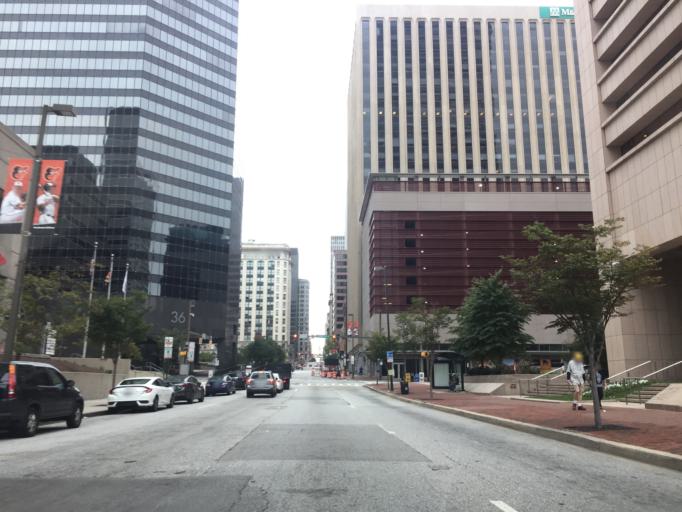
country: US
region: Maryland
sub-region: City of Baltimore
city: Baltimore
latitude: 39.2870
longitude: -76.6149
